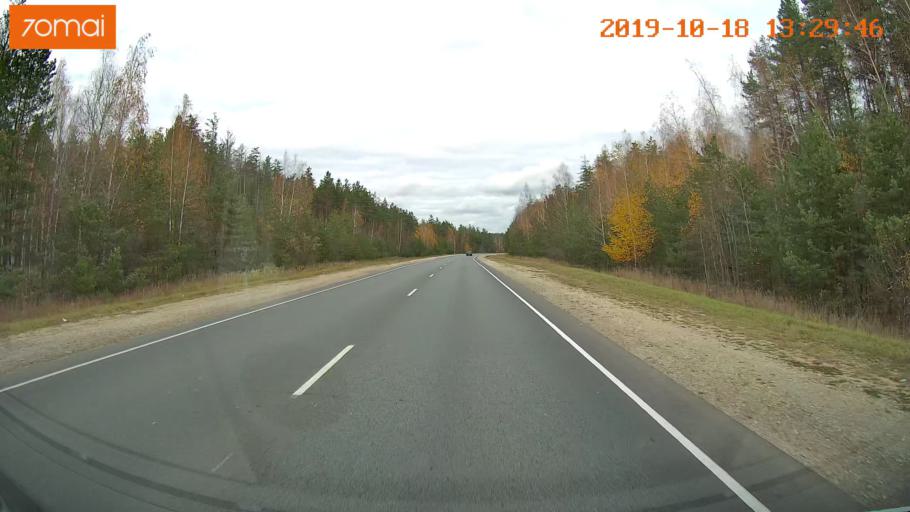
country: RU
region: Rjazan
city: Solotcha
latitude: 54.8001
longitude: 39.8772
